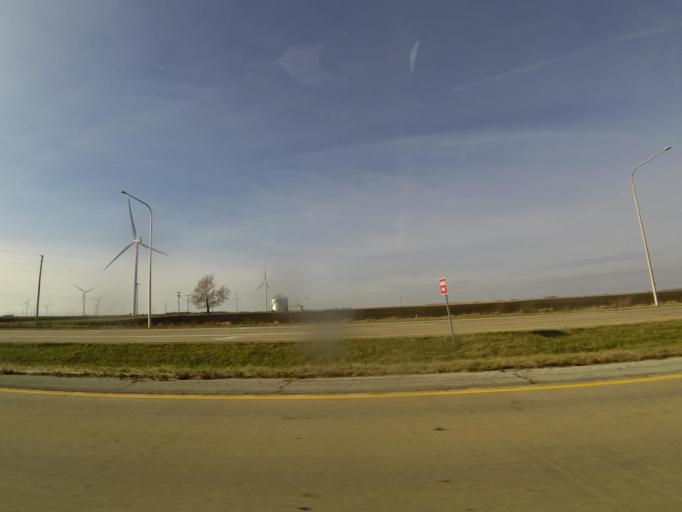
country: US
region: Illinois
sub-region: Macon County
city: Maroa
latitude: 40.0525
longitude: -88.9659
